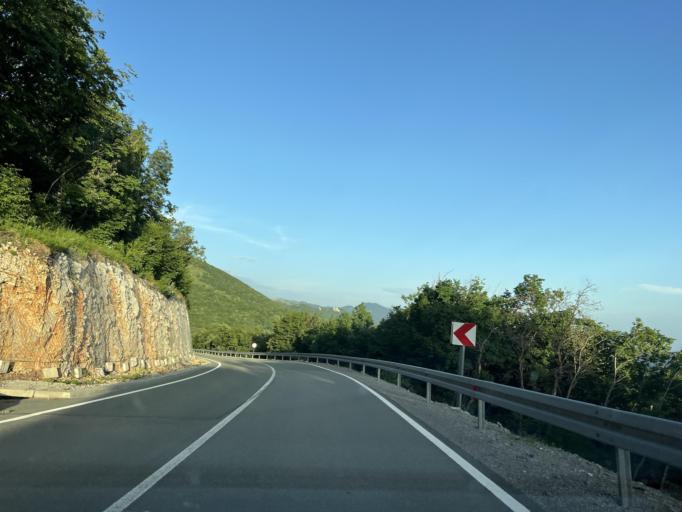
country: HR
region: Primorsko-Goranska
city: Cernik
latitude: 45.3927
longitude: 14.5541
